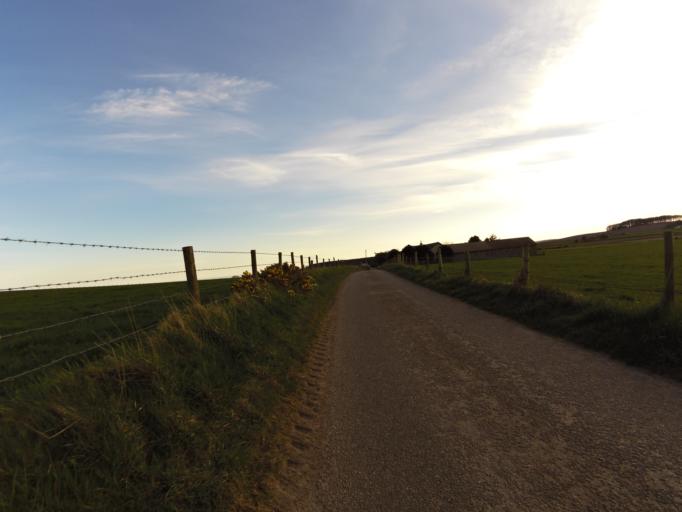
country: GB
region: Scotland
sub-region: Aberdeenshire
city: Stonehaven
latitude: 56.9341
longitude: -2.2246
